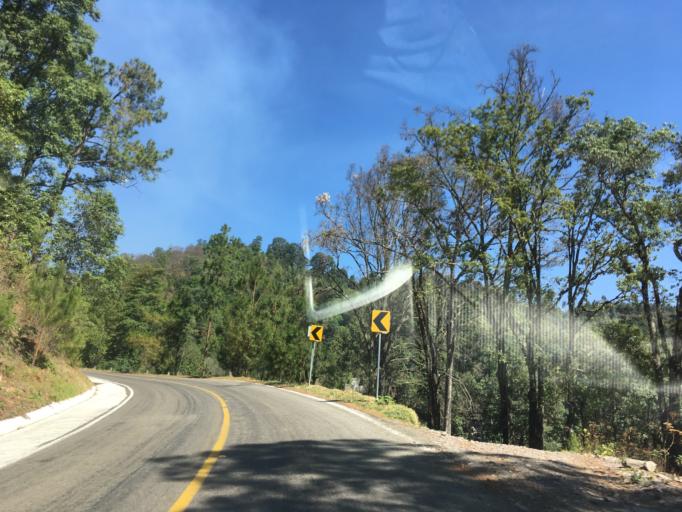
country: MX
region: Michoacan
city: Tzitzio
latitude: 19.6687
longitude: -100.9056
